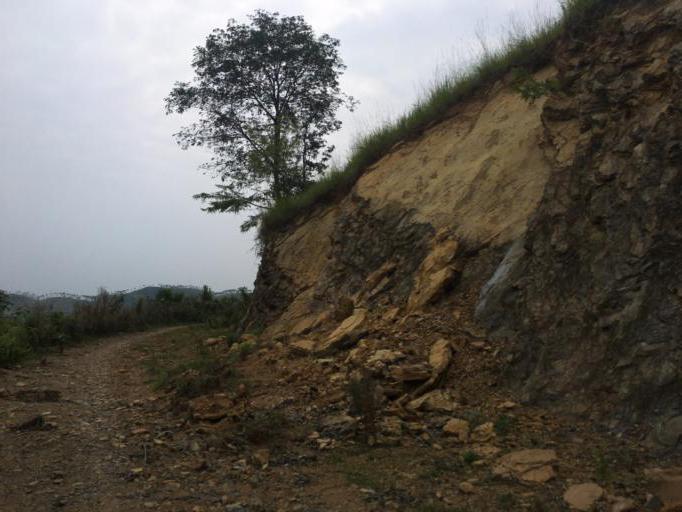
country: CN
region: Guizhou Sheng
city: Anshun
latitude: 25.4867
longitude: 105.9226
